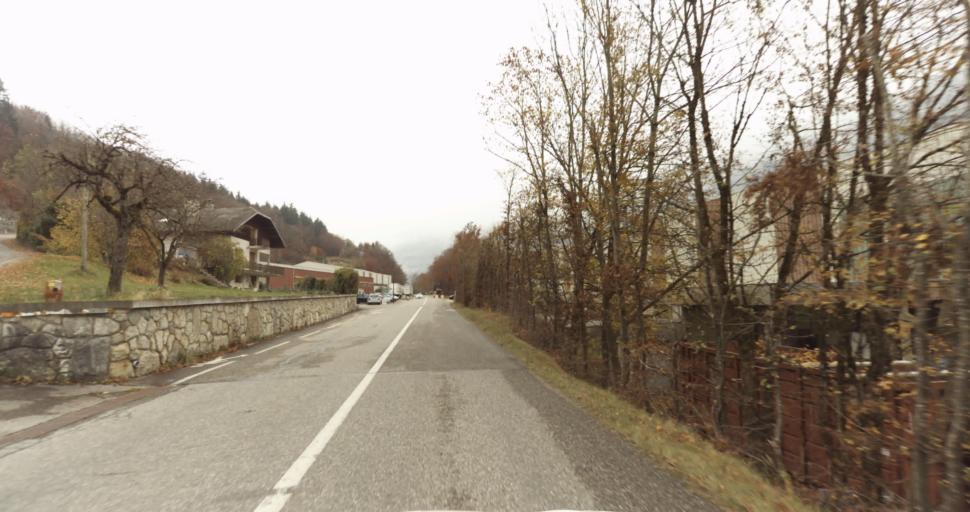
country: FR
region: Rhone-Alpes
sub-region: Departement de la Haute-Savoie
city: Gruffy
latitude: 45.7588
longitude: 6.0667
